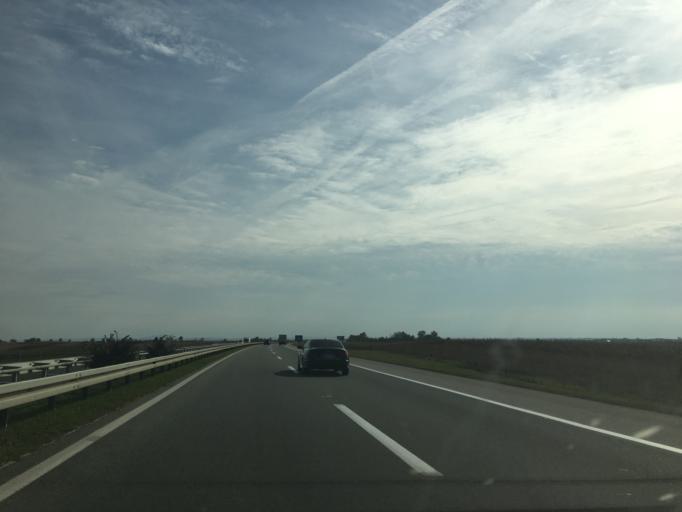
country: RS
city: Novi Banovci
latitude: 44.9278
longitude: 20.3007
